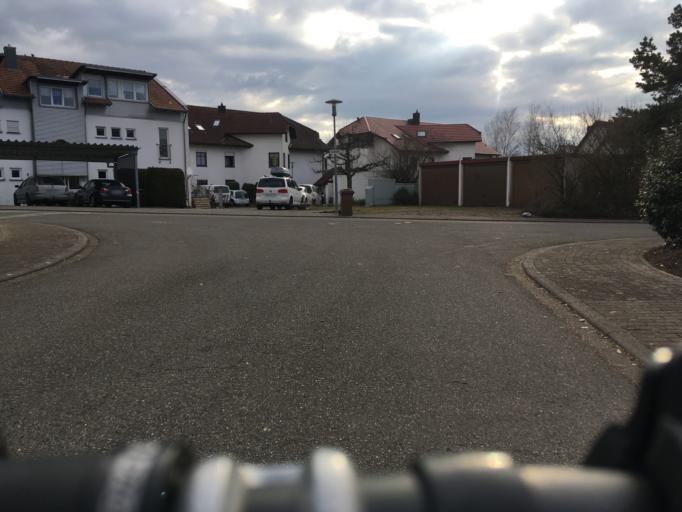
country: DE
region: Baden-Wuerttemberg
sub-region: Freiburg Region
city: Gottmadingen
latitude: 47.7341
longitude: 8.7696
